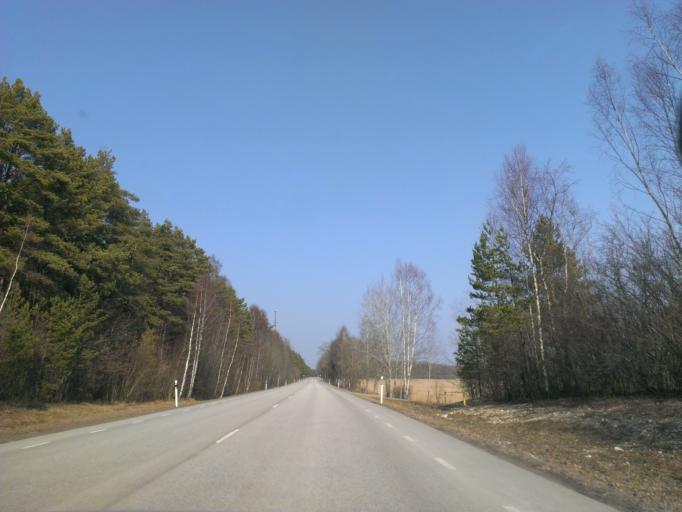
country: EE
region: Saare
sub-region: Orissaare vald
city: Orissaare
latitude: 58.5455
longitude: 23.0564
